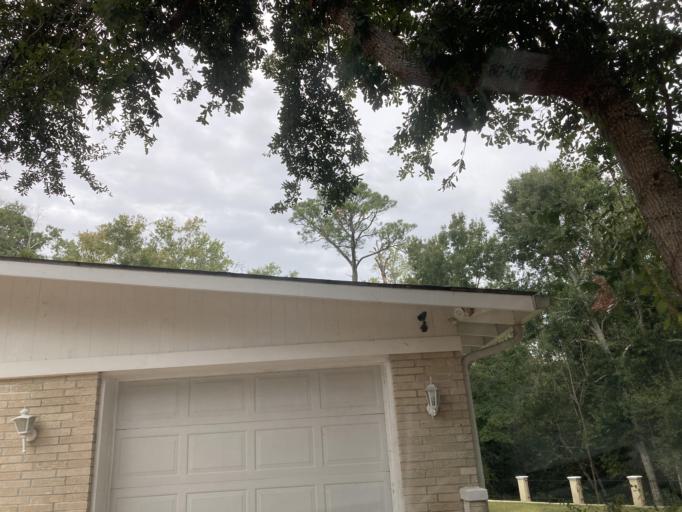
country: US
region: Mississippi
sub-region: Jackson County
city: Gulf Hills
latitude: 30.4292
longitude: -88.8350
